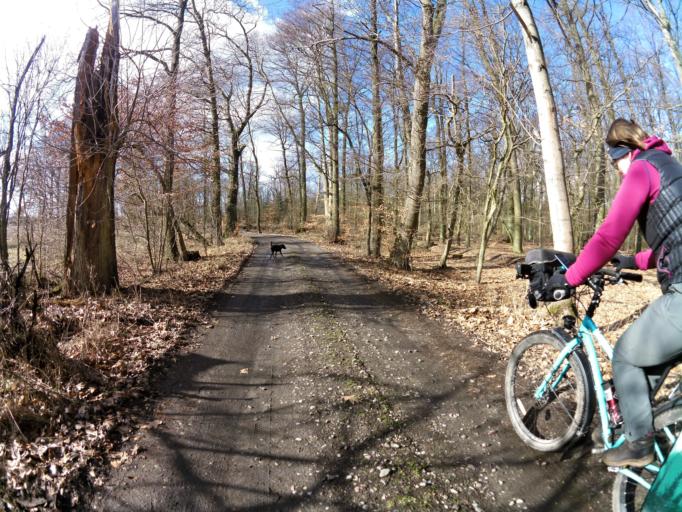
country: PL
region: West Pomeranian Voivodeship
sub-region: Powiat mysliborski
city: Debno
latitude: 52.7616
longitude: 14.7163
